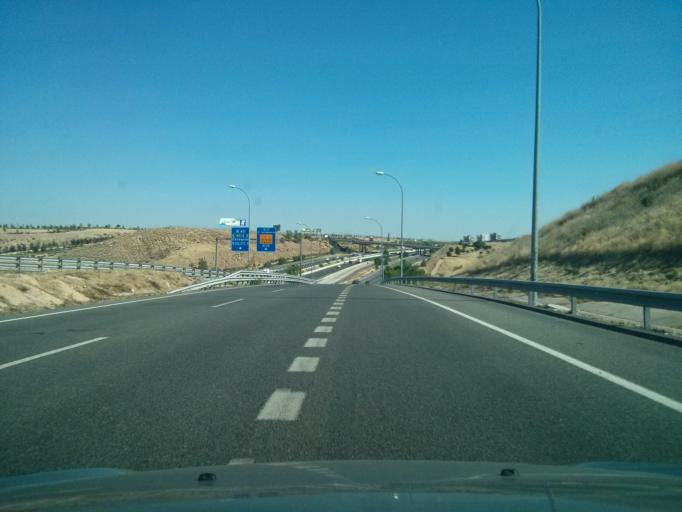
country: ES
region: Madrid
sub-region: Provincia de Madrid
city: Hortaleza
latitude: 40.4948
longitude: -3.6473
